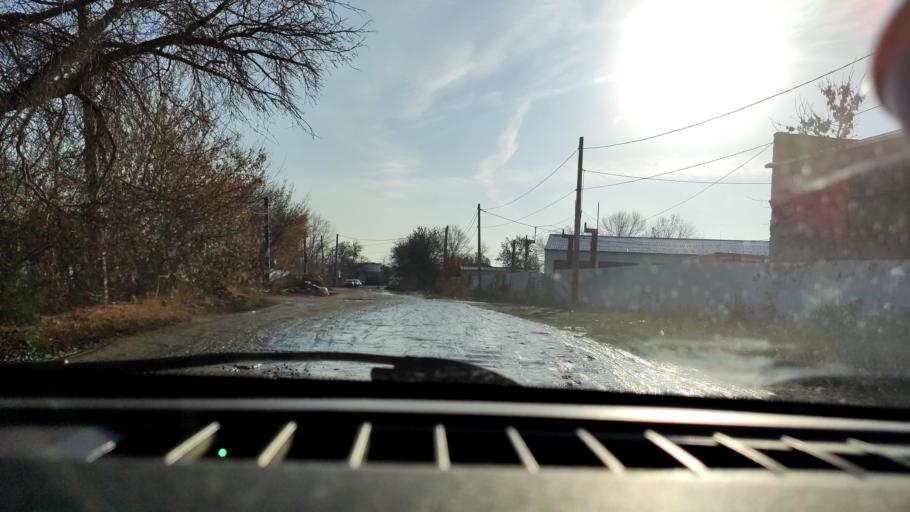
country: RU
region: Samara
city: Samara
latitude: 53.1177
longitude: 50.1143
